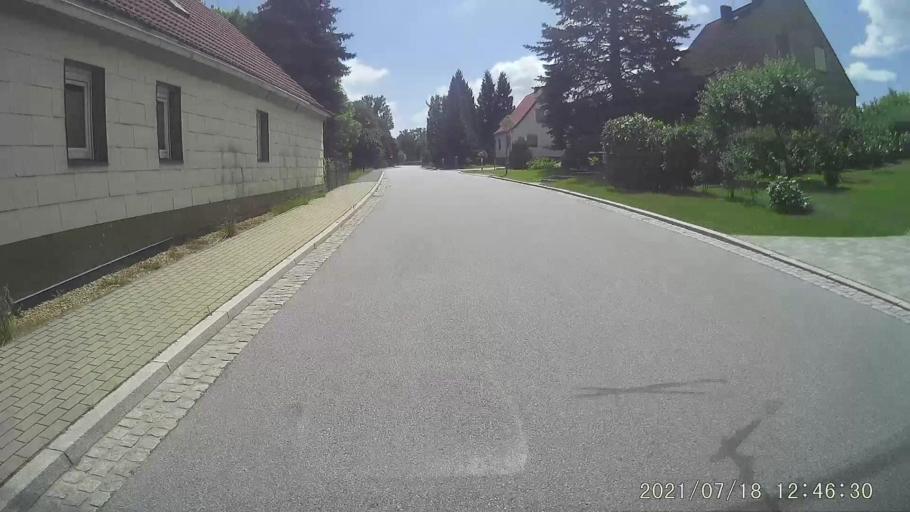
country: DE
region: Saxony
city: Reichenbach
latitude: 51.1928
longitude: 14.7882
